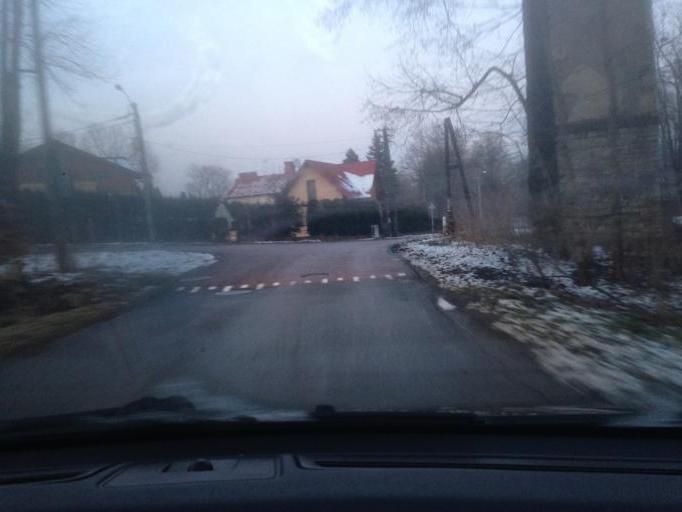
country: PL
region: Silesian Voivodeship
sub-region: Powiat bielski
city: Bystra
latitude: 49.7838
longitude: 19.0341
